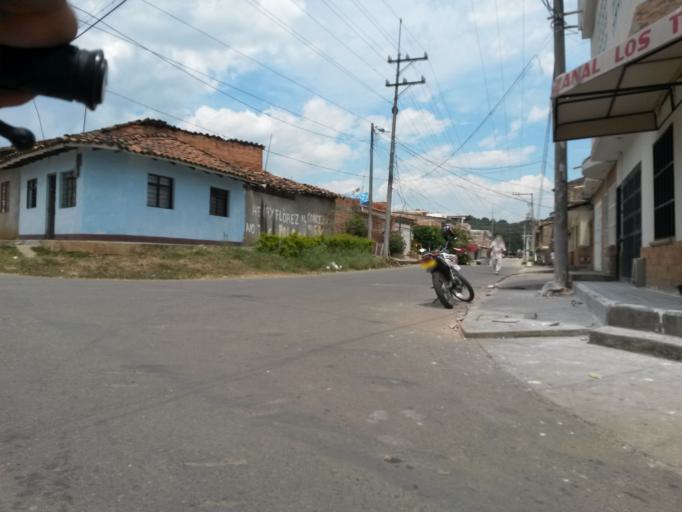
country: CO
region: Cauca
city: Santander de Quilichao
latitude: 3.0112
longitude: -76.4888
